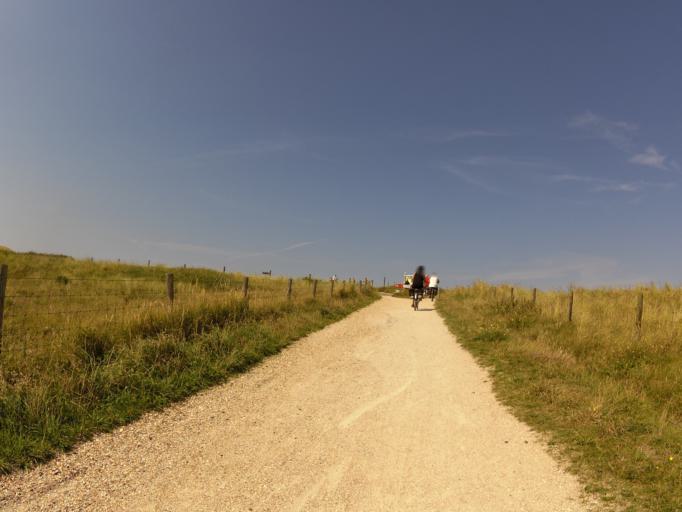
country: NL
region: North Holland
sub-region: Gemeente Schagen
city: Harenkarspel
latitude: 52.7739
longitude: 4.6636
